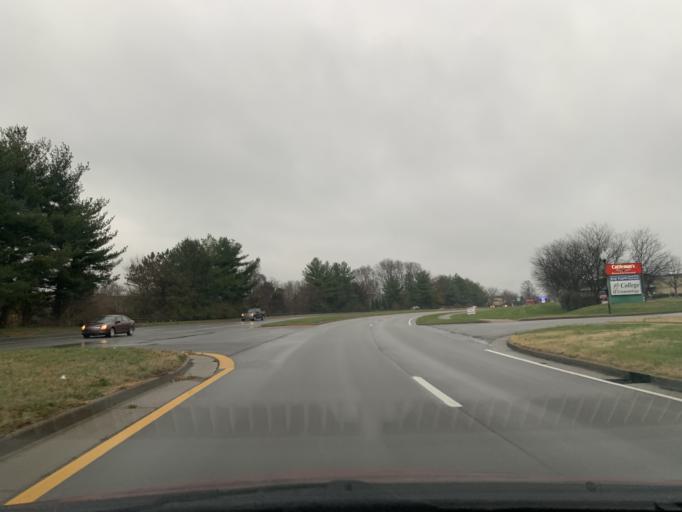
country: US
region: Kentucky
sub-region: Jefferson County
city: Hurstbourne Acres
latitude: 38.2080
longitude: -85.6015
